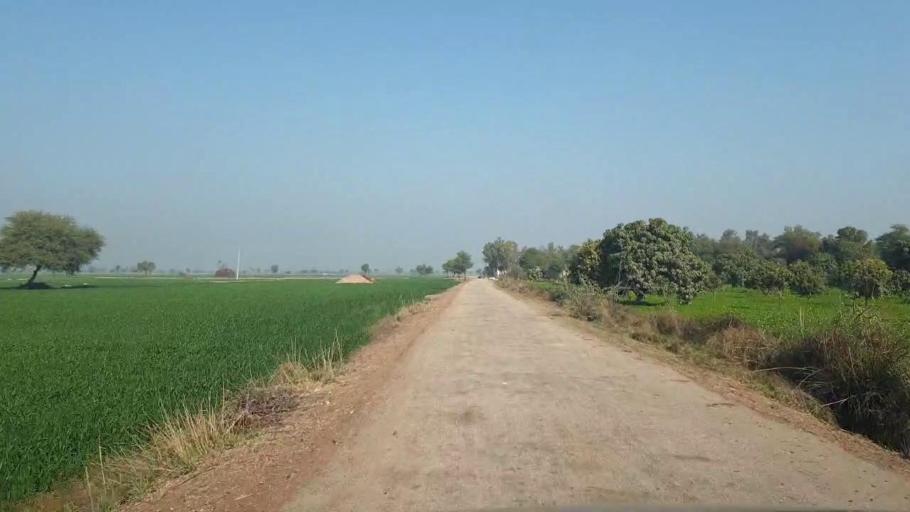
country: PK
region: Sindh
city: Shahdadpur
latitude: 25.9713
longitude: 68.5874
